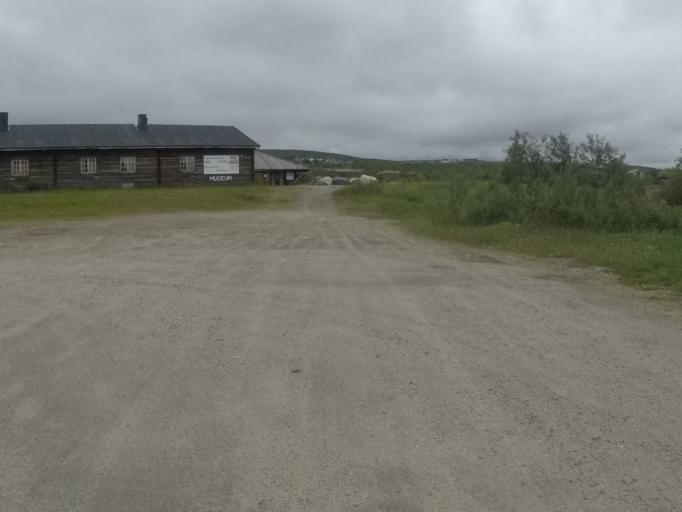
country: NO
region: Finnmark Fylke
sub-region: Kautokeino
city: Kautokeino
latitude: 69.0091
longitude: 23.0473
